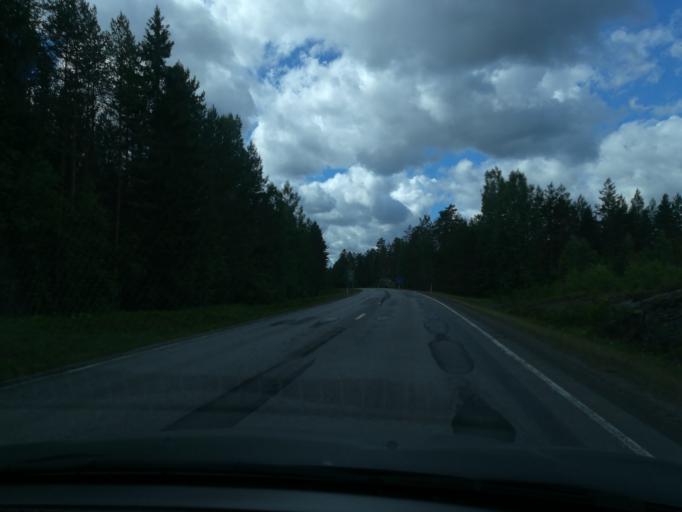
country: FI
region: Southern Savonia
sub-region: Mikkeli
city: Ristiina
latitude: 61.4499
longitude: 27.2593
